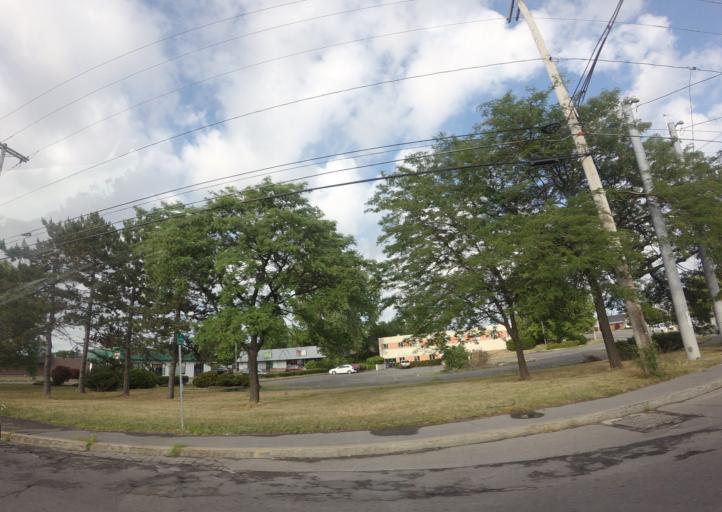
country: US
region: New York
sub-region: Onondaga County
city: East Syracuse
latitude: 43.0431
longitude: -76.0678
